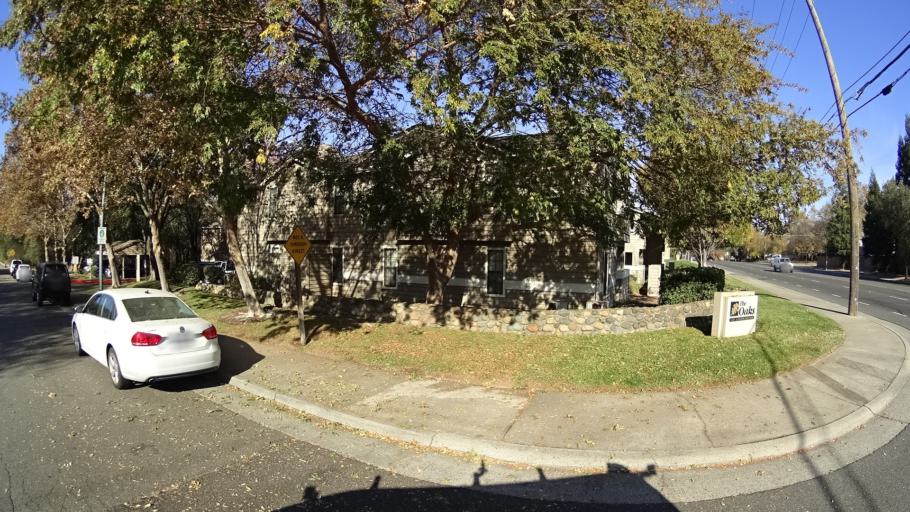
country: US
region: California
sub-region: Sacramento County
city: Citrus Heights
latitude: 38.6855
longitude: -121.2906
